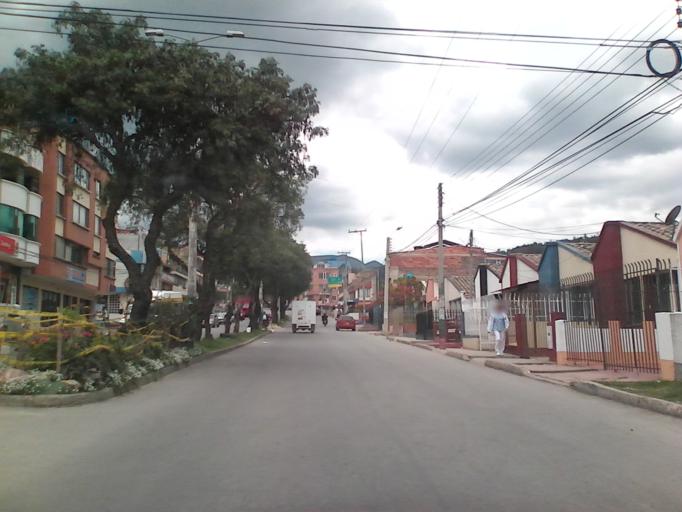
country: CO
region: Boyaca
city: Duitama
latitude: 5.8247
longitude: -73.0421
